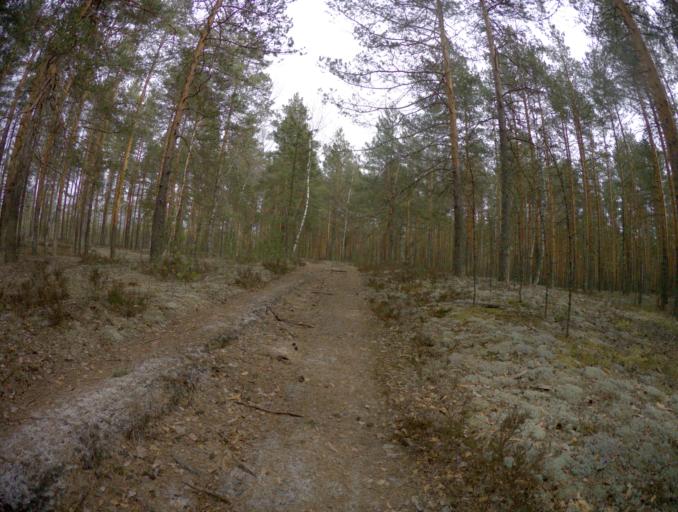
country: RU
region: Vladimir
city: Raduzhnyy
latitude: 55.9362
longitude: 40.2871
